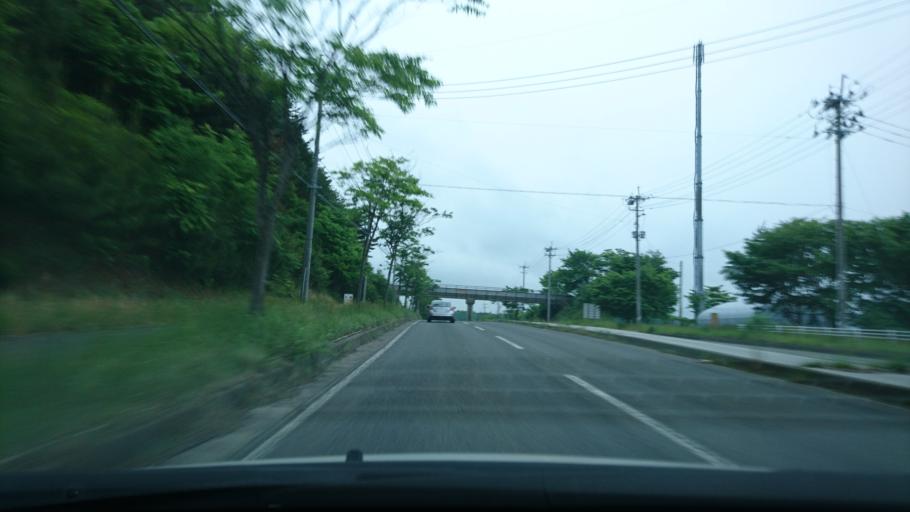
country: JP
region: Iwate
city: Ichinoseki
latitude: 38.9170
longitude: 141.1590
